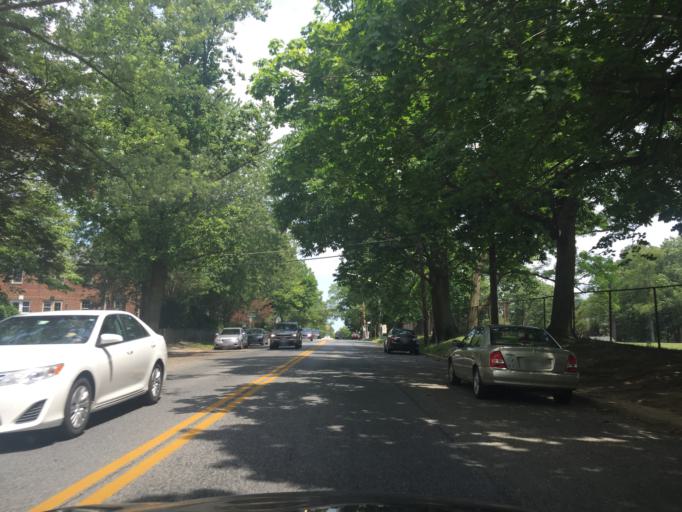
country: US
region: Maryland
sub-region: Baltimore County
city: Towson
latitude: 39.3831
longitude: -76.6154
